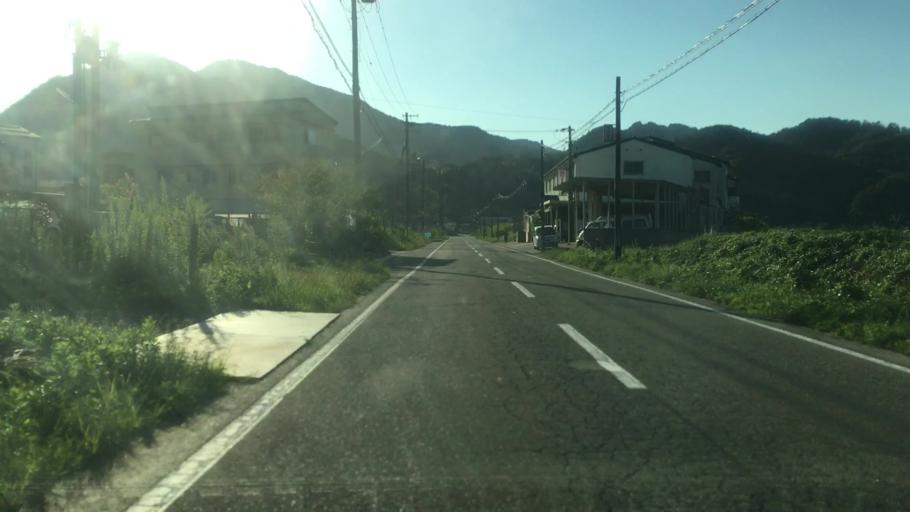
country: JP
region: Hyogo
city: Toyooka
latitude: 35.6190
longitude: 134.8186
